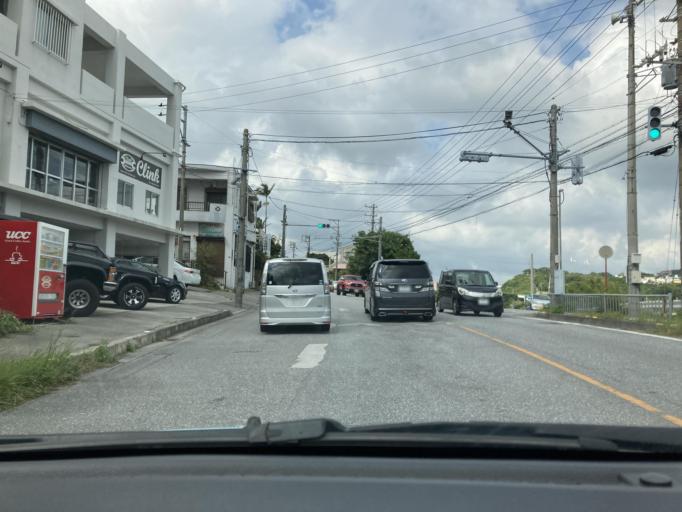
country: JP
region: Okinawa
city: Chatan
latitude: 26.2859
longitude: 127.7863
